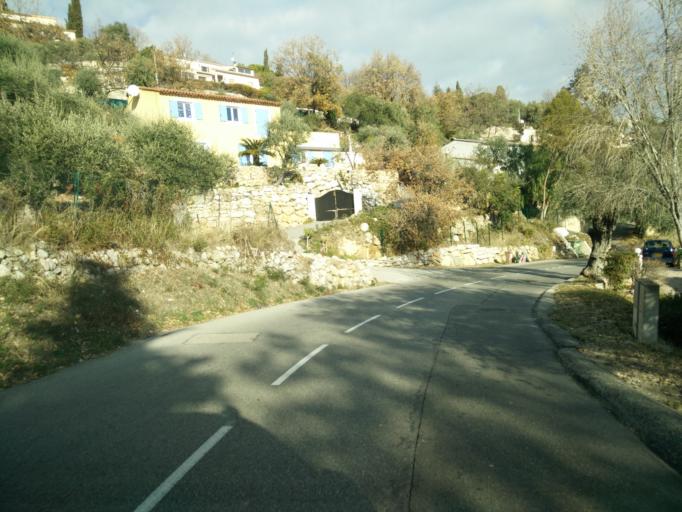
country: FR
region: Provence-Alpes-Cote d'Azur
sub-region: Departement des Alpes-Maritimes
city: Carros
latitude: 43.7871
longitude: 7.1835
